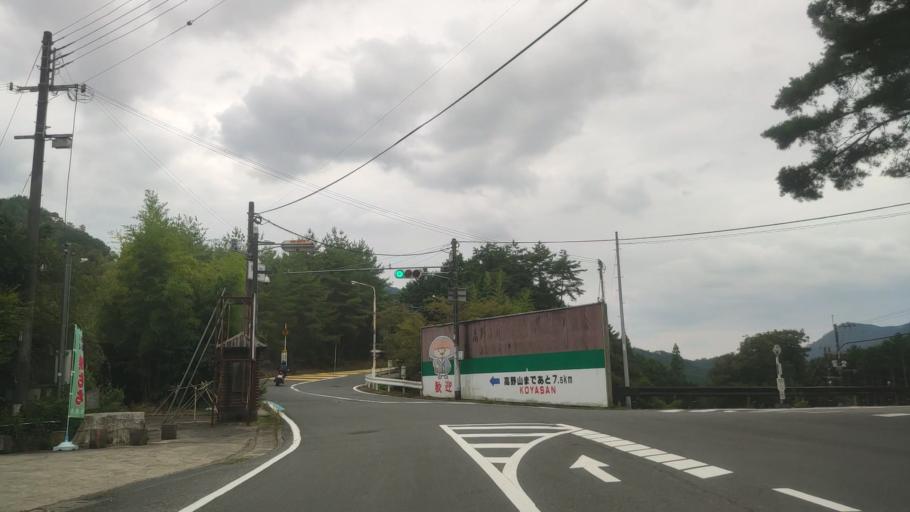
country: JP
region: Wakayama
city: Koya
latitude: 34.2194
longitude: 135.5372
